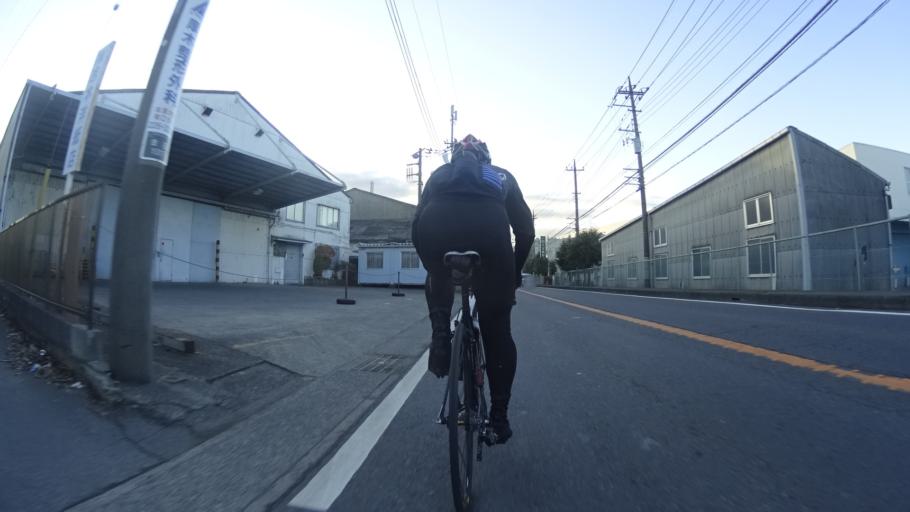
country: JP
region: Kanagawa
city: Atsugi
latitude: 35.4568
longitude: 139.3683
